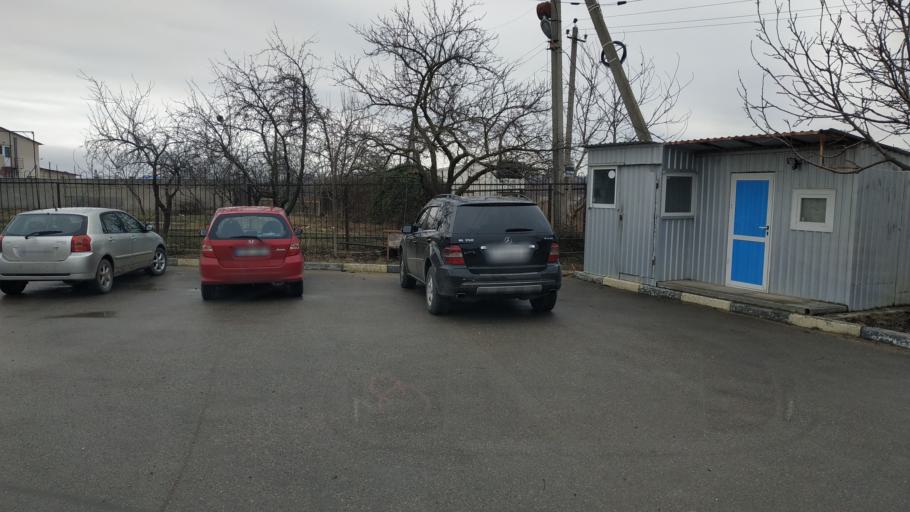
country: MD
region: Laloveni
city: Ialoveni
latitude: 46.9397
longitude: 28.7763
